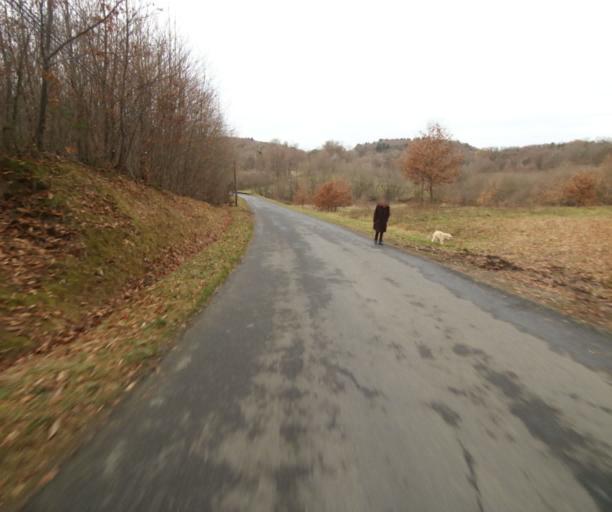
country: FR
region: Limousin
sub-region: Departement de la Correze
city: Chameyrat
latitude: 45.2361
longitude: 1.6893
